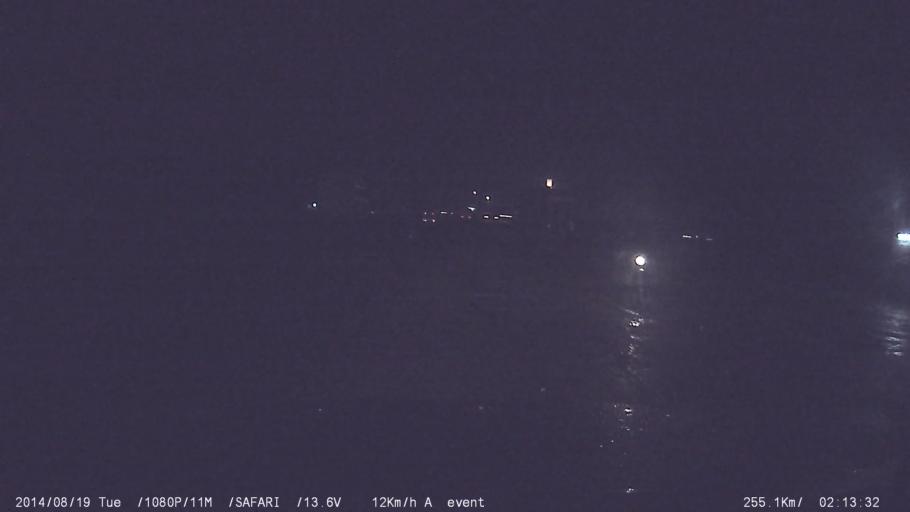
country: IN
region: Tamil Nadu
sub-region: Coimbatore
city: Madukkarai
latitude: 10.8878
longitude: 76.9172
